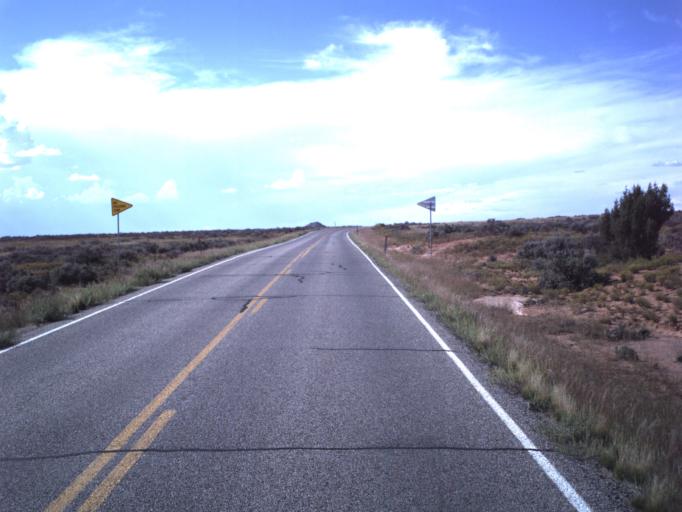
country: US
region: Utah
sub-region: Grand County
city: Moab
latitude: 38.5275
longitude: -109.7479
